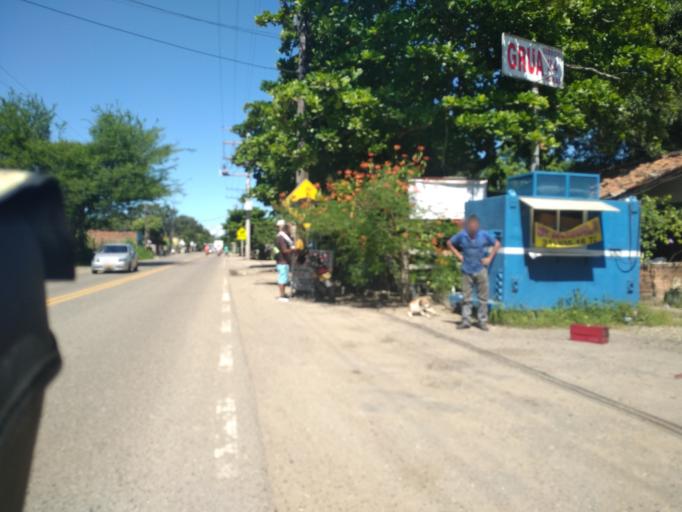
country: CO
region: Cundinamarca
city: Puerto Salgar
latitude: 5.4700
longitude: -74.6502
